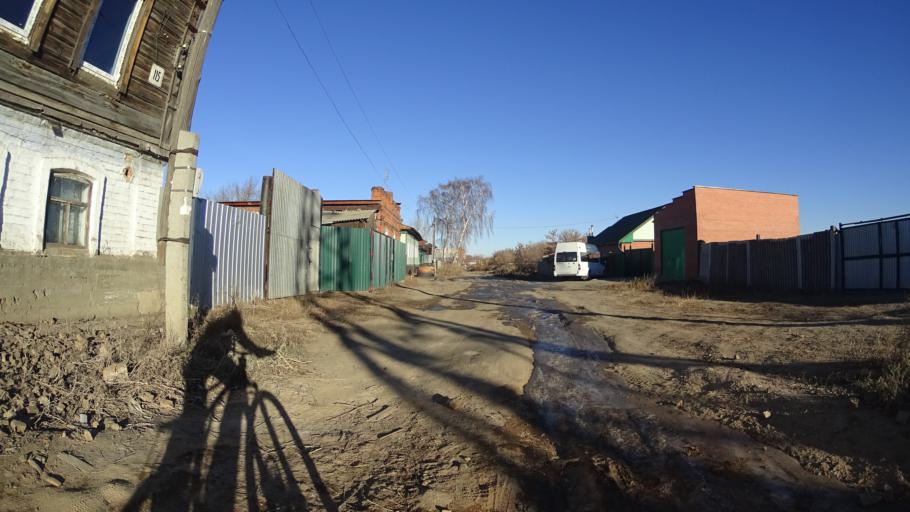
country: RU
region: Chelyabinsk
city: Troitsk
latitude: 54.0814
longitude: 61.5675
